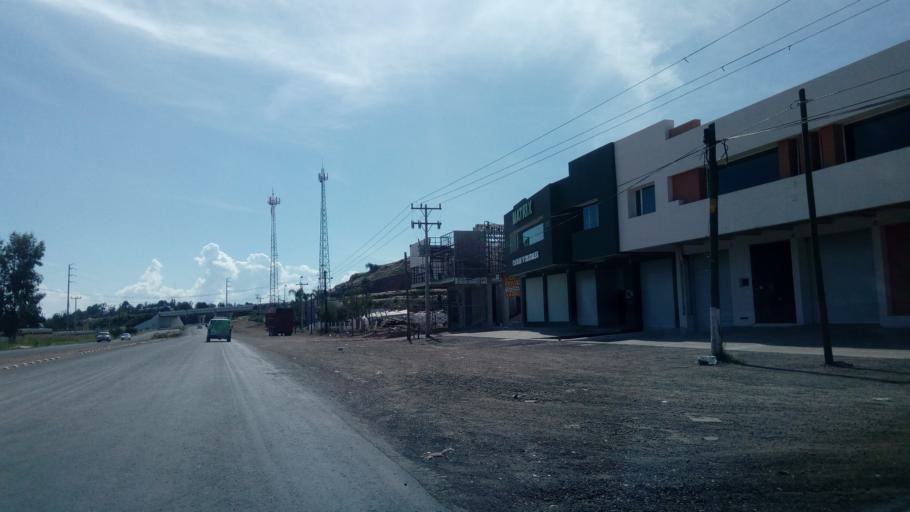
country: MX
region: Durango
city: Victoria de Durango
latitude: 24.0717
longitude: -104.6574
